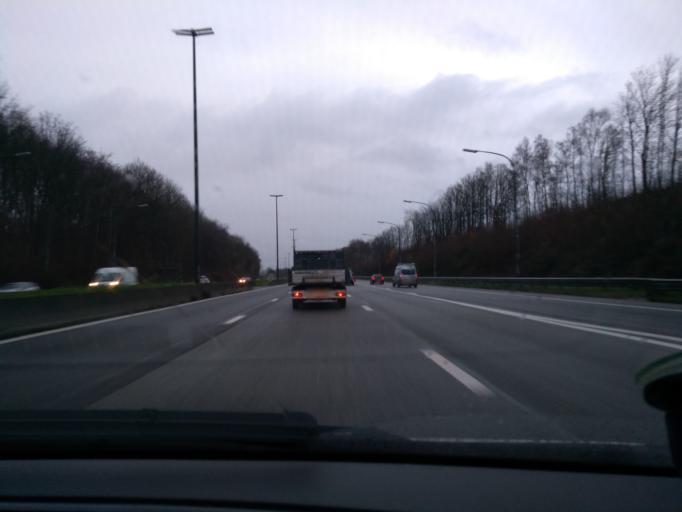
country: BE
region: Wallonia
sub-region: Province du Hainaut
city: Chapelle-lez-Herlaimont
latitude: 50.4836
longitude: 4.2759
